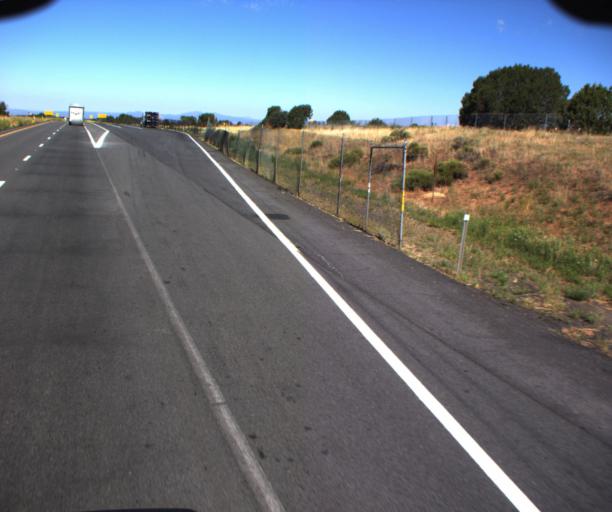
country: US
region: Arizona
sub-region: Coconino County
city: Williams
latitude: 35.2216
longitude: -112.3146
